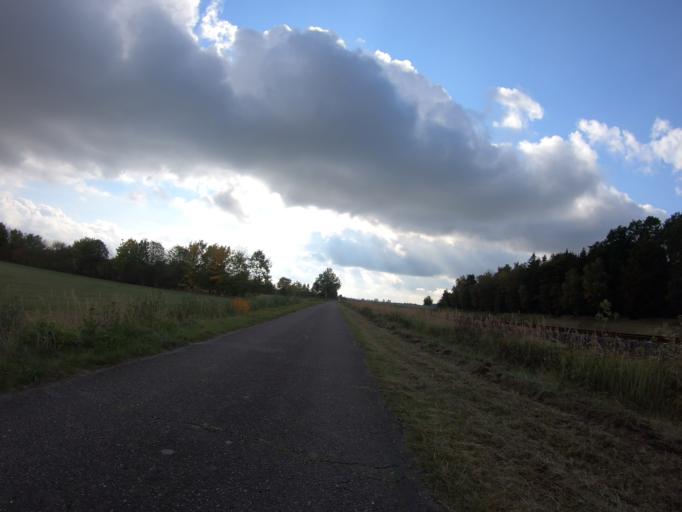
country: DE
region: Lower Saxony
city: Wahrenholz
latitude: 52.5886
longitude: 10.6095
